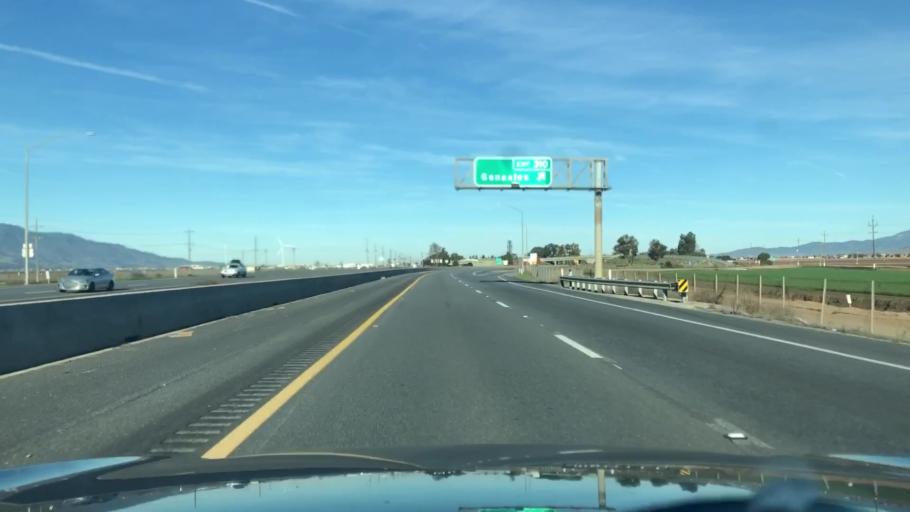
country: US
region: California
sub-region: Monterey County
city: Gonzales
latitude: 36.4890
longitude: -121.4228
